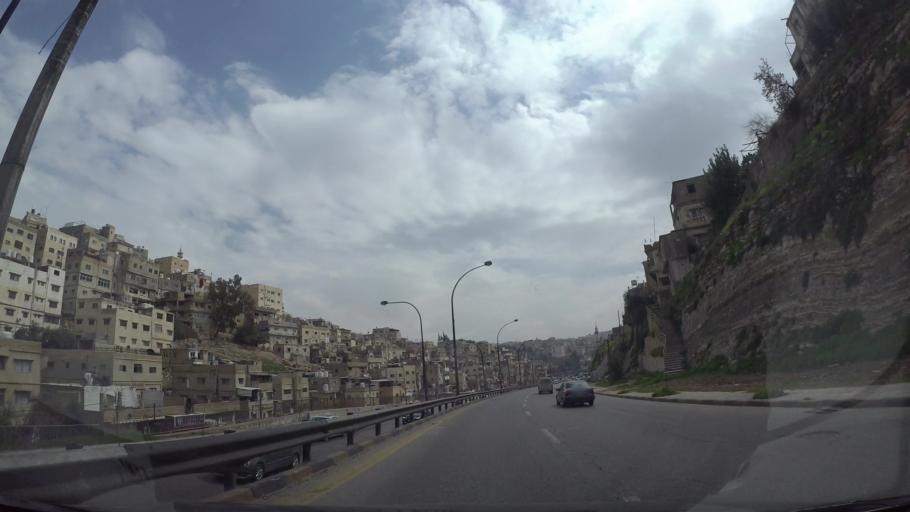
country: JO
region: Amman
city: Amman
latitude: 31.9644
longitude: 35.9541
